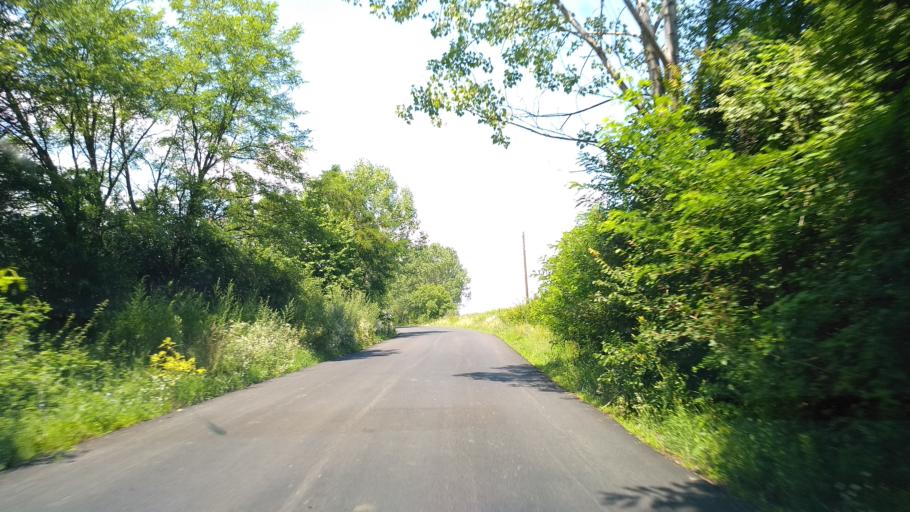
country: RO
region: Hunedoara
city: Berca
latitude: 45.6482
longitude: 23.0242
